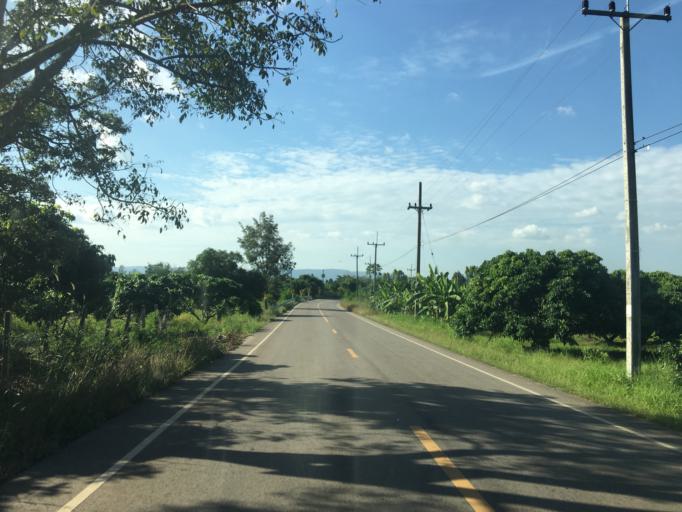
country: TH
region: Chiang Rai
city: Pa Daet
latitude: 19.4328
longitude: 100.0113
